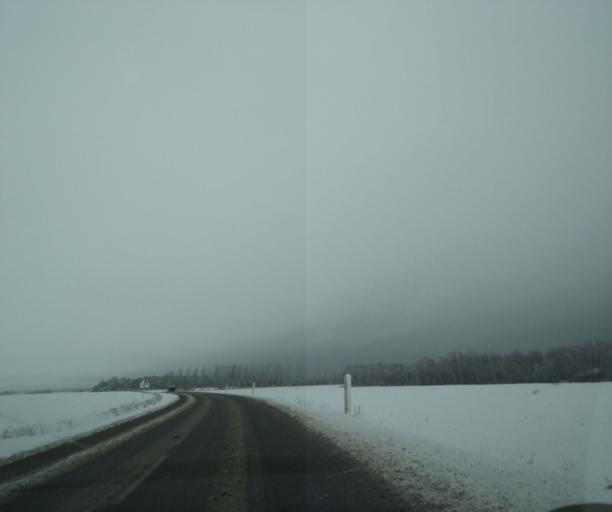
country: FR
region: Champagne-Ardenne
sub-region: Departement de la Haute-Marne
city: Wassy
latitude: 48.5546
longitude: 4.9264
